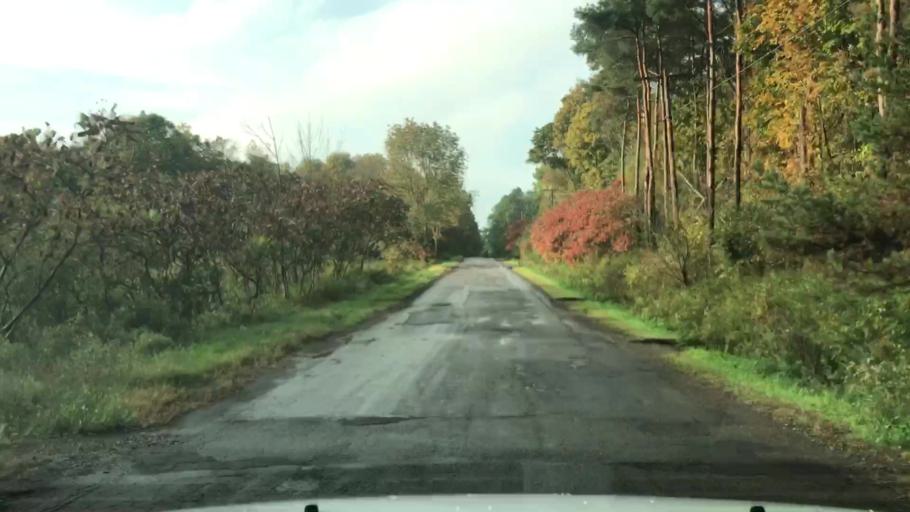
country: US
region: New York
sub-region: Cattaraugus County
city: Little Valley
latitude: 42.3073
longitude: -78.7169
